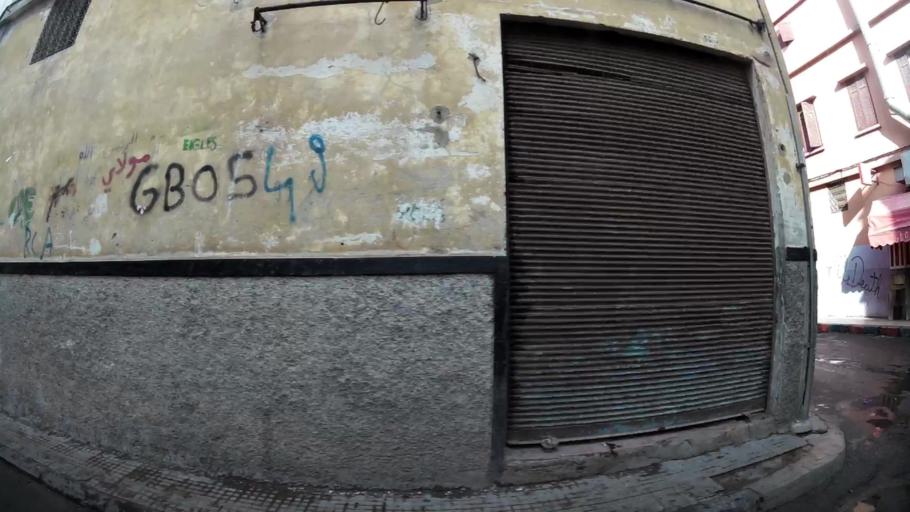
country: MA
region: Grand Casablanca
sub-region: Casablanca
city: Casablanca
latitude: 33.5520
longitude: -7.5918
